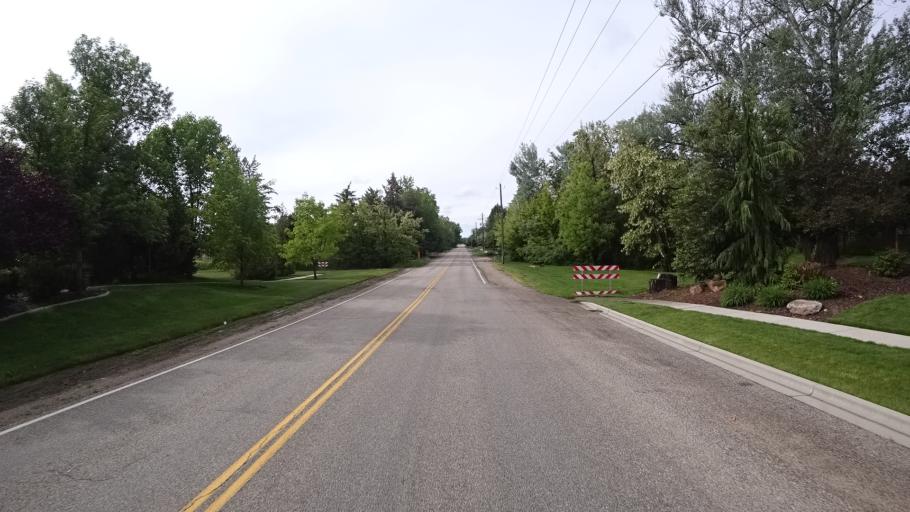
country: US
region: Idaho
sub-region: Ada County
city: Eagle
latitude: 43.7034
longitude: -116.3791
